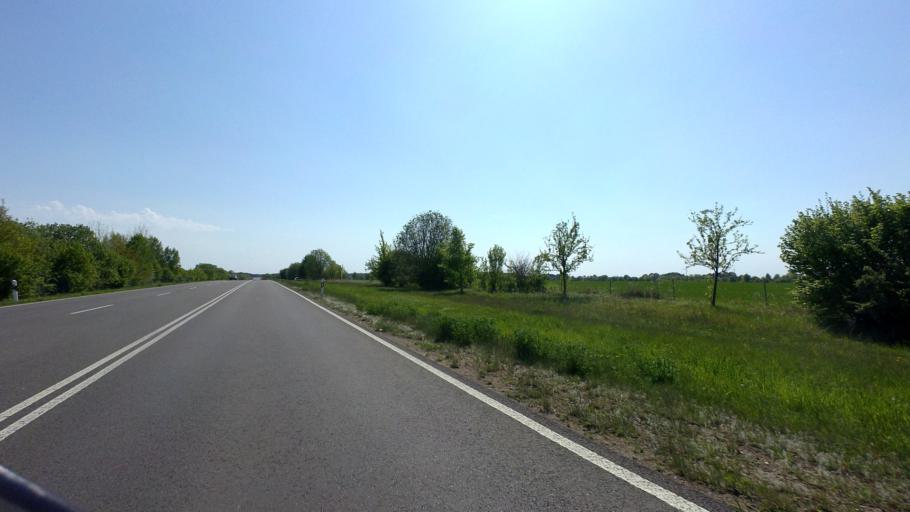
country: DE
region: Brandenburg
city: Beeskow
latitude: 52.1772
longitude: 14.2167
